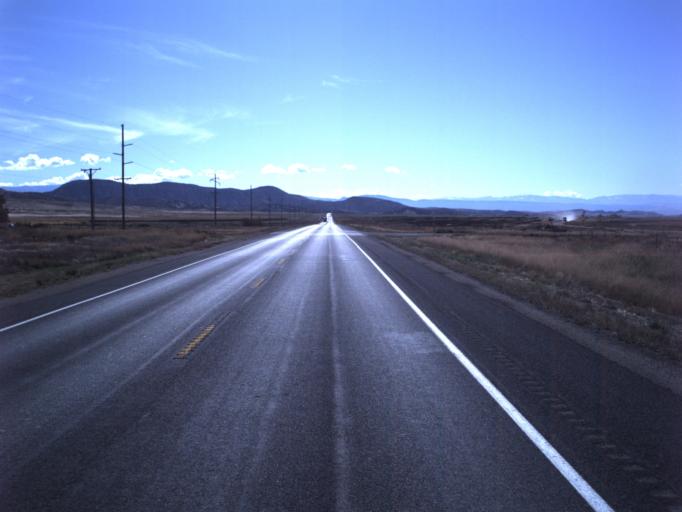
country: US
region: Utah
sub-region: Sanpete County
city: Gunnison
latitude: 39.2623
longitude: -111.8663
